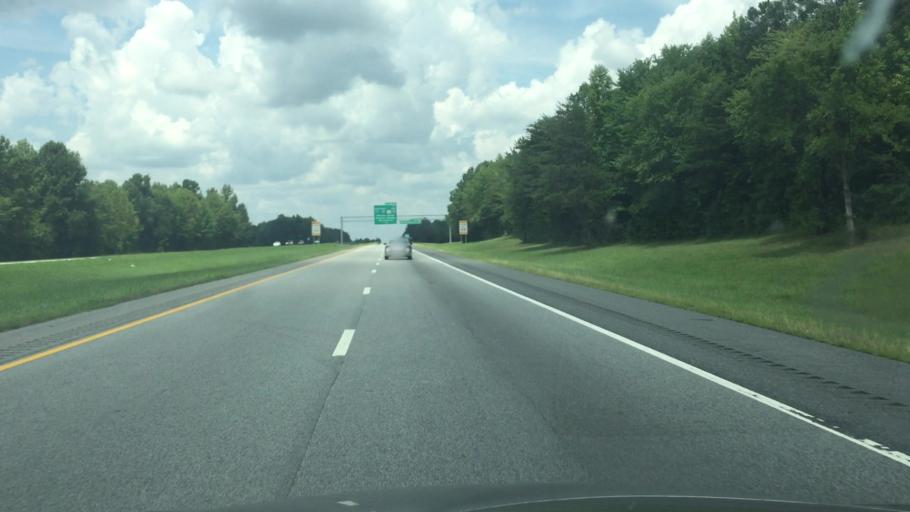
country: US
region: North Carolina
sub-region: Guilford County
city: Pleasant Garden
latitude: 35.9811
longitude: -79.8229
